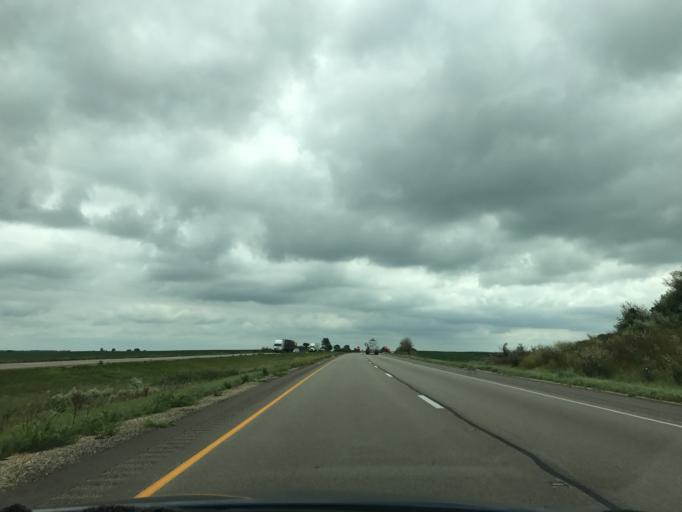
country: US
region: Illinois
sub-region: Bureau County
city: Walnut
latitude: 41.3935
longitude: -89.6431
